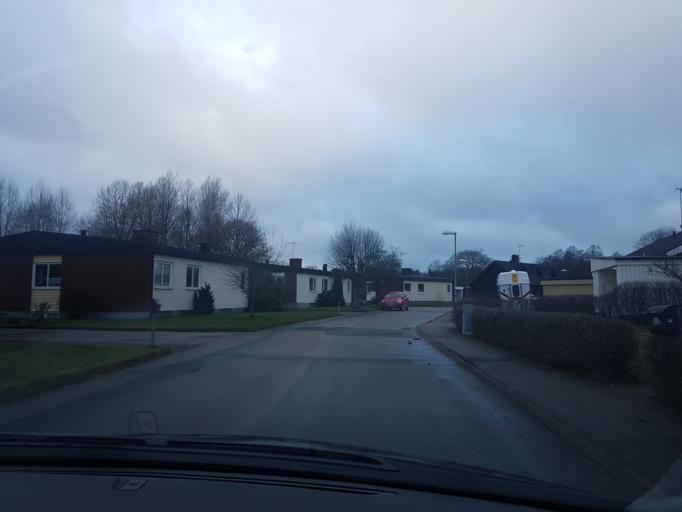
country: SE
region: Joenkoeping
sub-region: Vetlanda Kommun
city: Vetlanda
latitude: 57.4344
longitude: 15.0781
